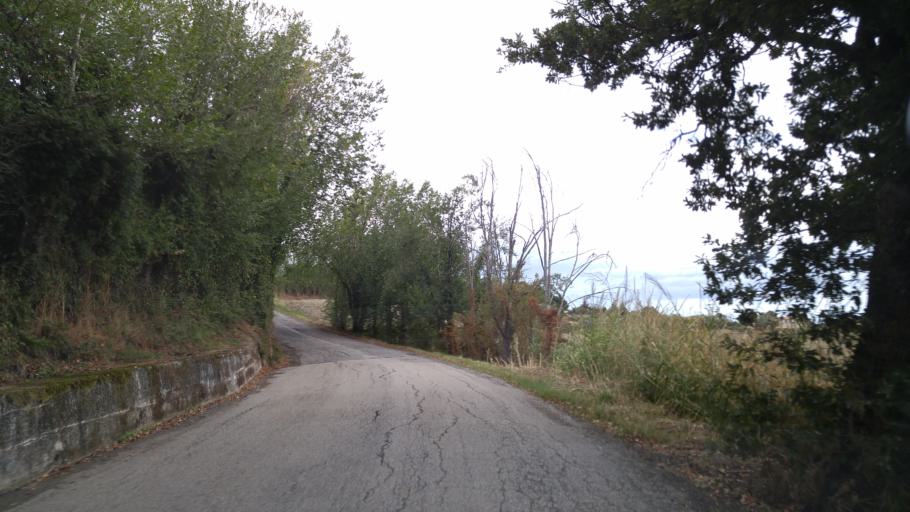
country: IT
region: The Marches
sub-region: Provincia di Pesaro e Urbino
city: Mombaroccio
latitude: 43.7908
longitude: 12.8766
